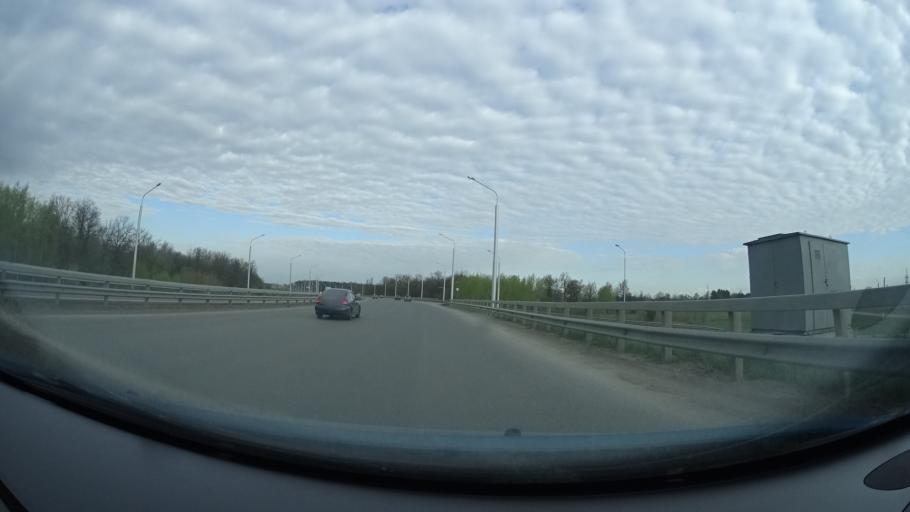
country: RU
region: Bashkortostan
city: Ufa
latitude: 54.7756
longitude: 55.9492
